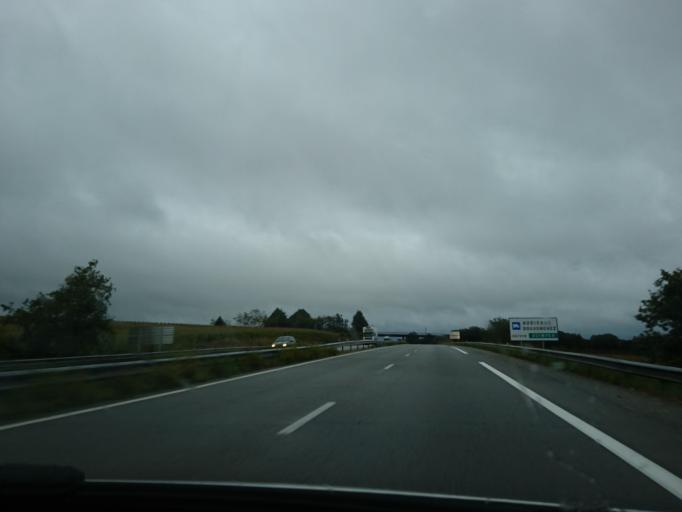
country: FR
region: Brittany
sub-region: Departement du Finistere
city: Chateaulin
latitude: 48.2301
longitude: -4.0941
